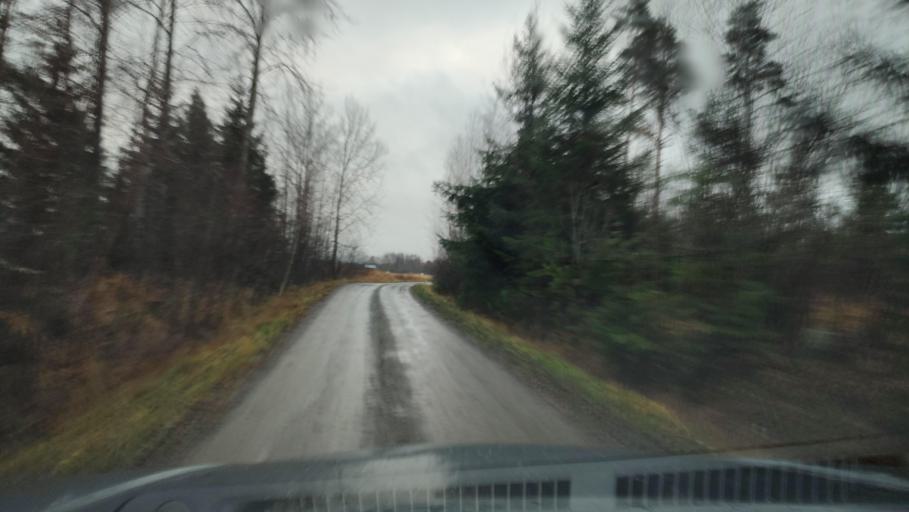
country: FI
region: Ostrobothnia
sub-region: Sydosterbotten
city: Kristinestad
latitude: 62.2431
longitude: 21.4871
